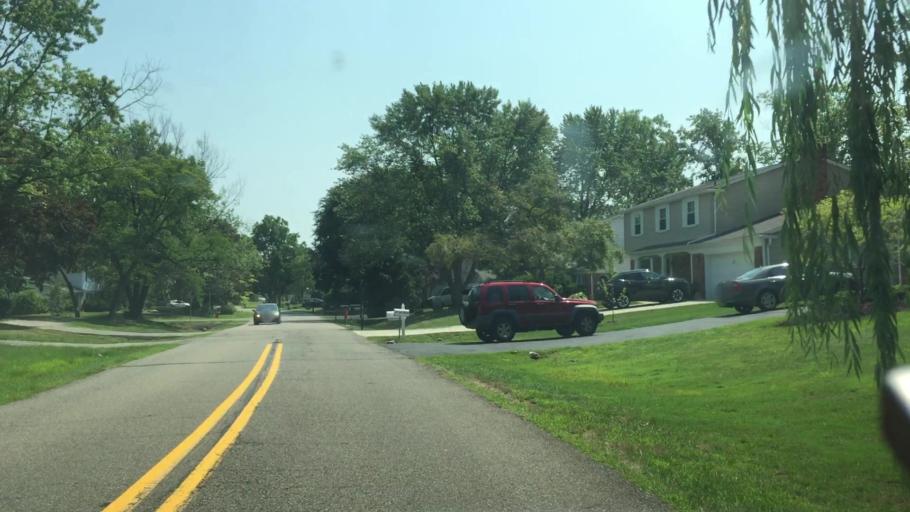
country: US
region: Michigan
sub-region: Oakland County
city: West Bloomfield Township
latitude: 42.5311
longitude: -83.3548
